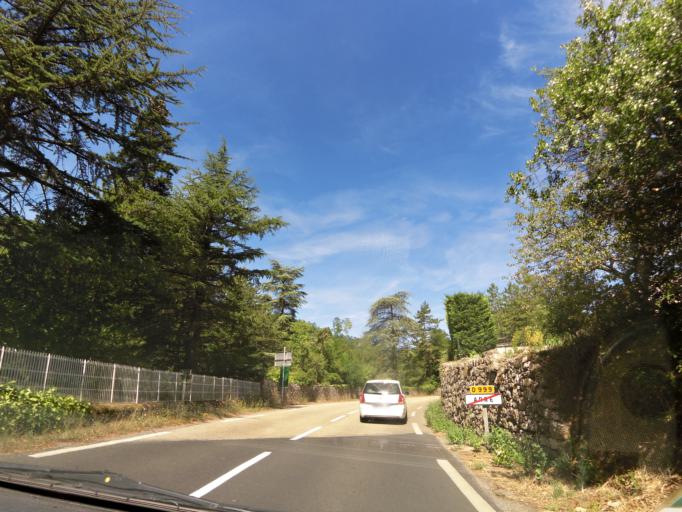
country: FR
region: Languedoc-Roussillon
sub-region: Departement du Gard
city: Aveze
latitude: 43.9689
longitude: 3.5147
